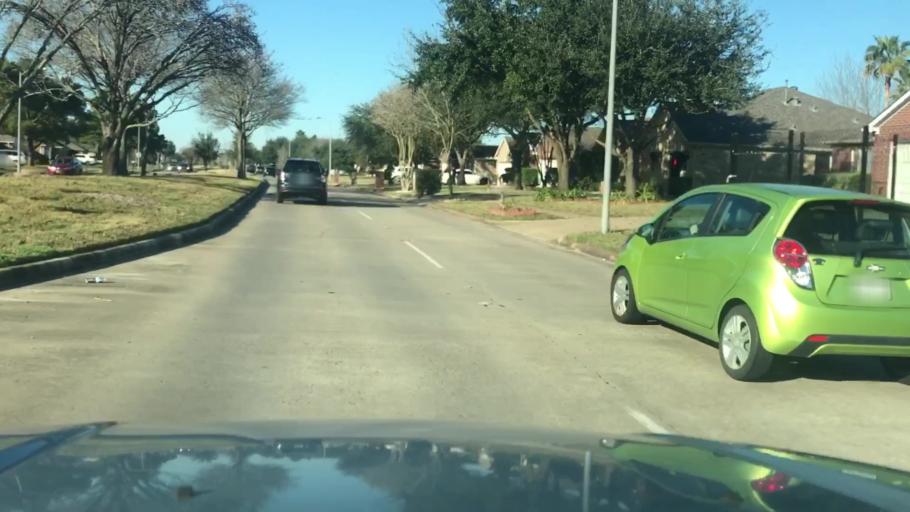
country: US
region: Texas
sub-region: Harris County
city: Katy
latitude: 29.8200
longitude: -95.7523
